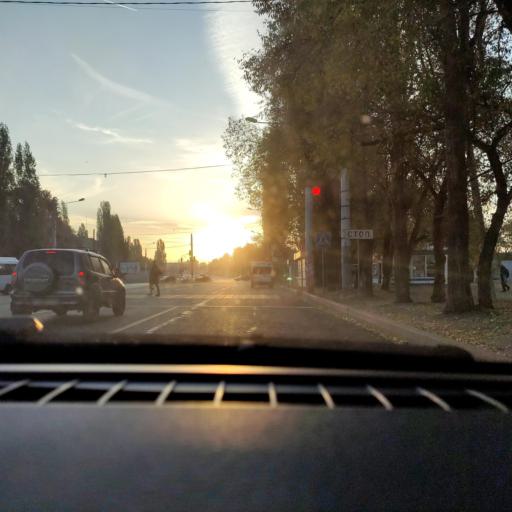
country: RU
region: Voronezj
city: Maslovka
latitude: 51.6006
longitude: 39.2421
